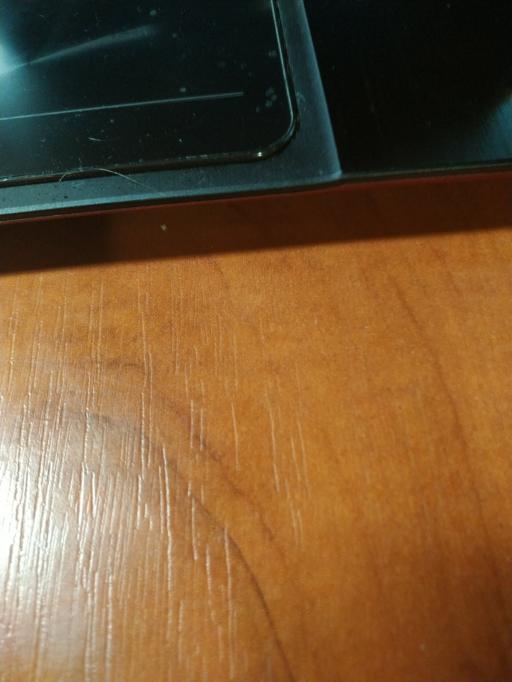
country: RU
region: Tverskaya
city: Likhoslavl'
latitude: 57.1841
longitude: 35.5855
